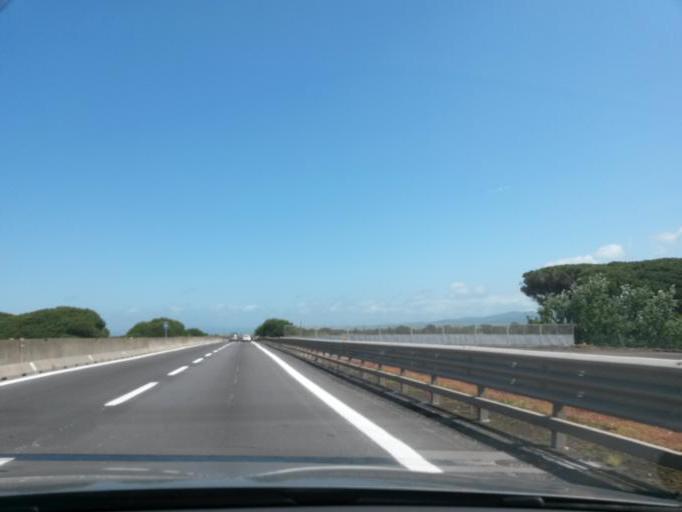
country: IT
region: Tuscany
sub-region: Provincia di Livorno
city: Donoratico
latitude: 43.1504
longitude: 10.5557
